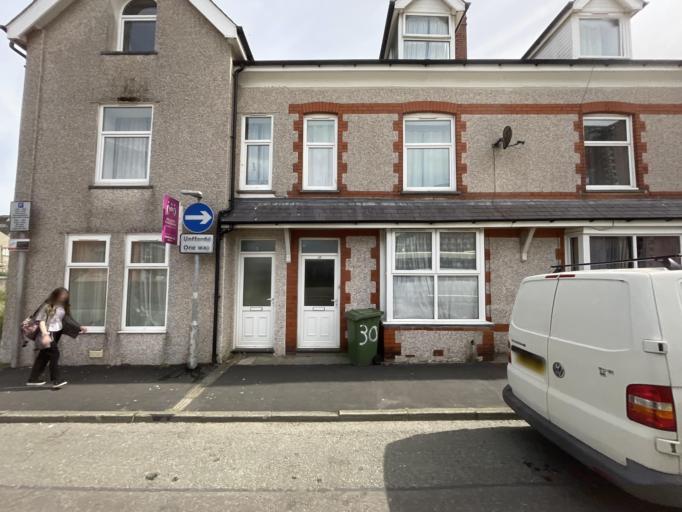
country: GB
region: Wales
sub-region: Gwynedd
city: Bangor
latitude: 53.2236
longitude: -4.1324
